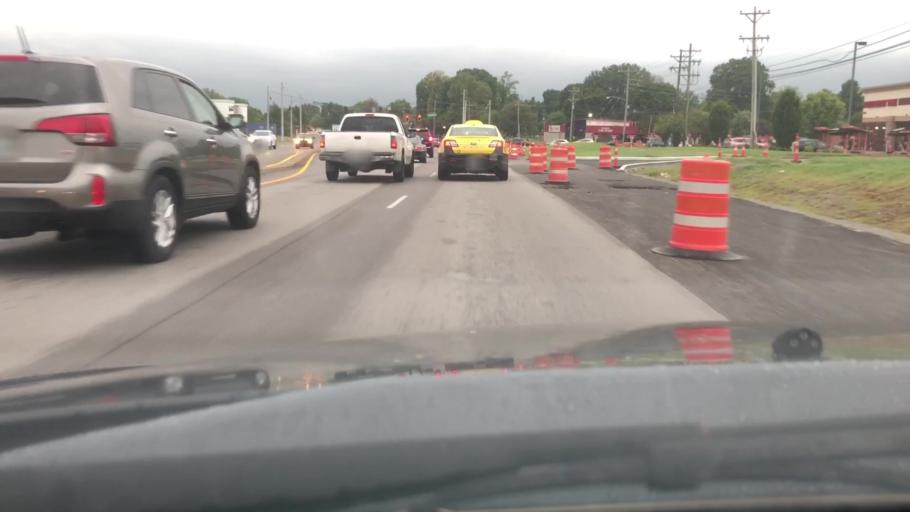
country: US
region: Kentucky
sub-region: Jefferson County
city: Hurstbourne Acres
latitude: 38.2146
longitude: -85.5895
